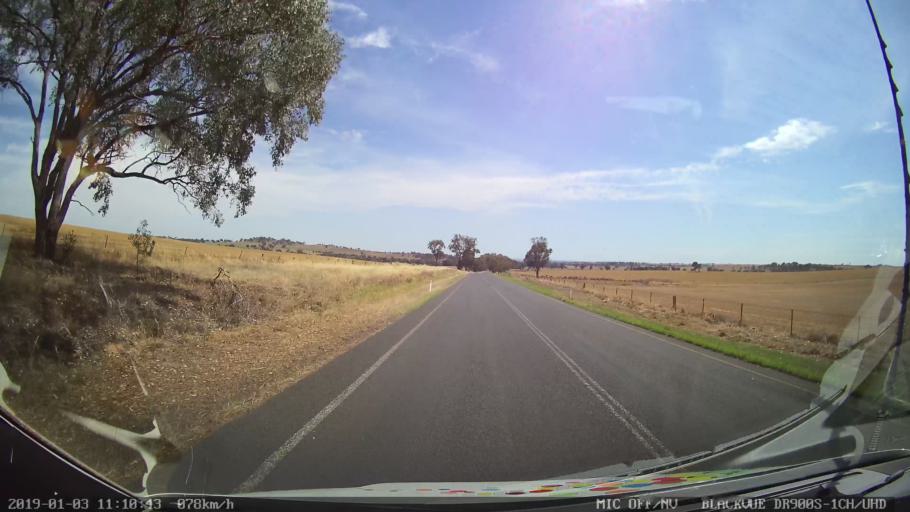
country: AU
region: New South Wales
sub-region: Young
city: Young
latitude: -34.2237
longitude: 148.2589
